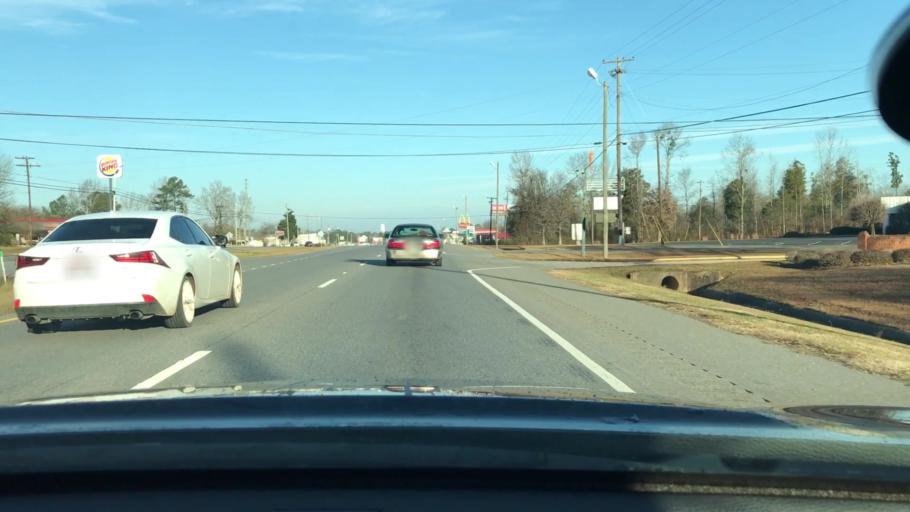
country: US
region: Alabama
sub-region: Talladega County
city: Childersburg
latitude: 33.2610
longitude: -86.3480
